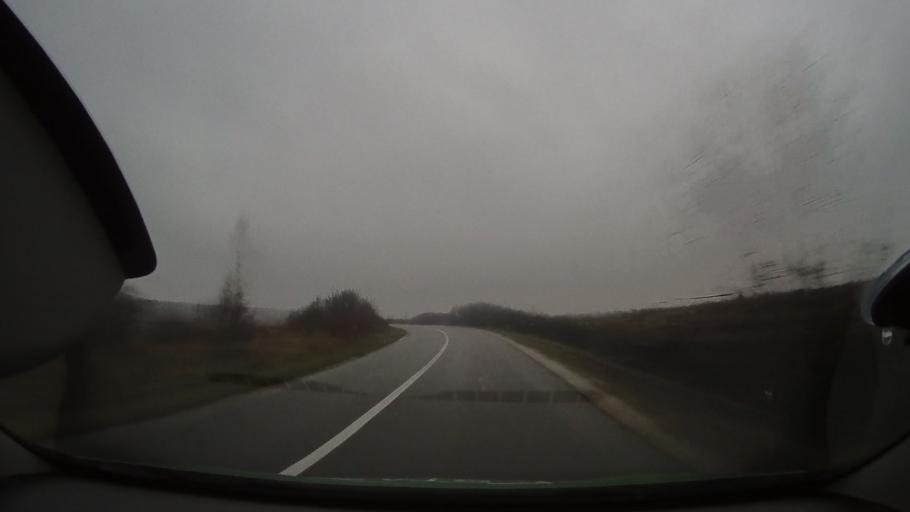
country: RO
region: Arad
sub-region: Comuna Craiova
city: Craiova
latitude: 46.5405
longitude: 21.9572
